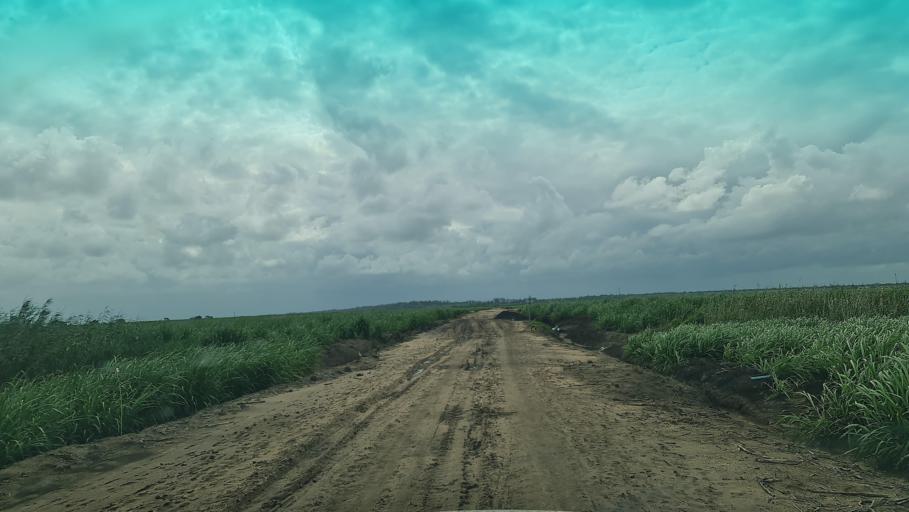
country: MZ
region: Maputo
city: Manhica
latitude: -25.4524
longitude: 32.8214
